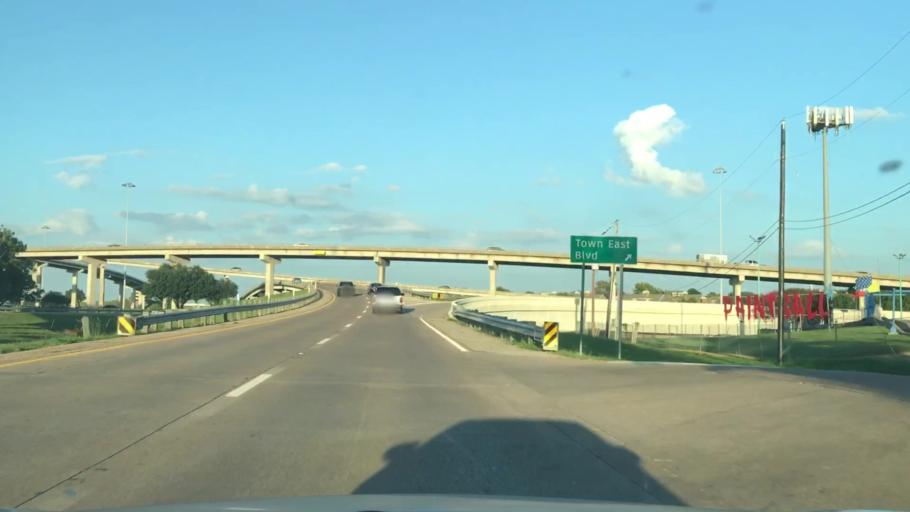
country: US
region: Texas
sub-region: Dallas County
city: Mesquite
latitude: 32.8210
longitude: -96.6316
